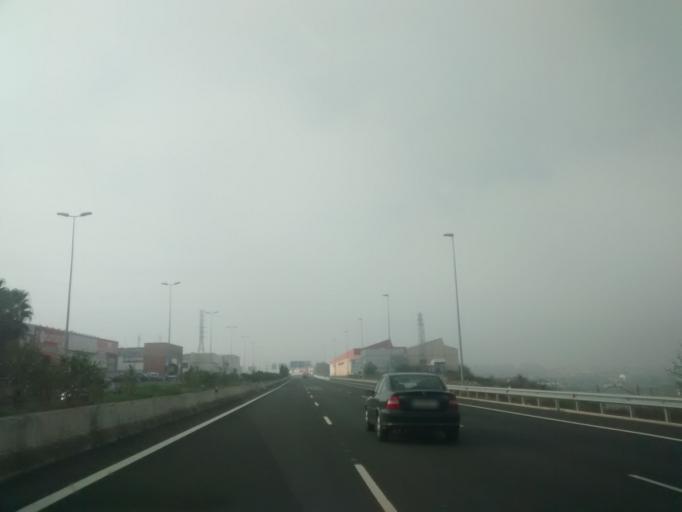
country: ES
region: La Rioja
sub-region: Provincia de La Rioja
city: Villamediana de Iregua
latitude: 42.4590
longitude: -2.3936
